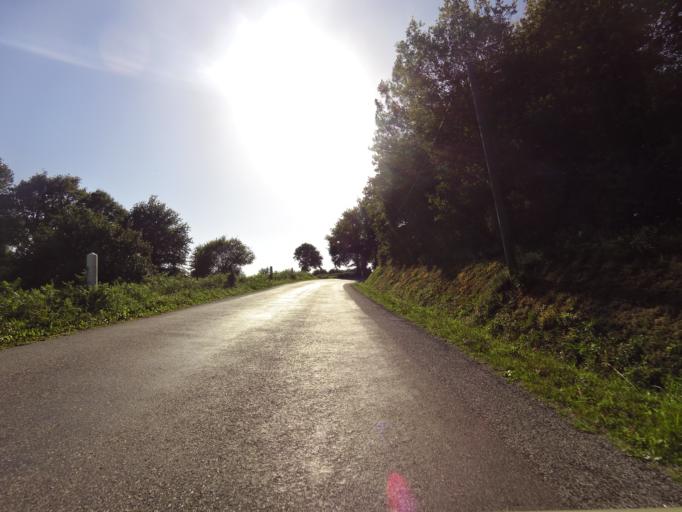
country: FR
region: Brittany
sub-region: Departement du Morbihan
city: Limerzel
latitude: 47.6312
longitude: -2.3435
